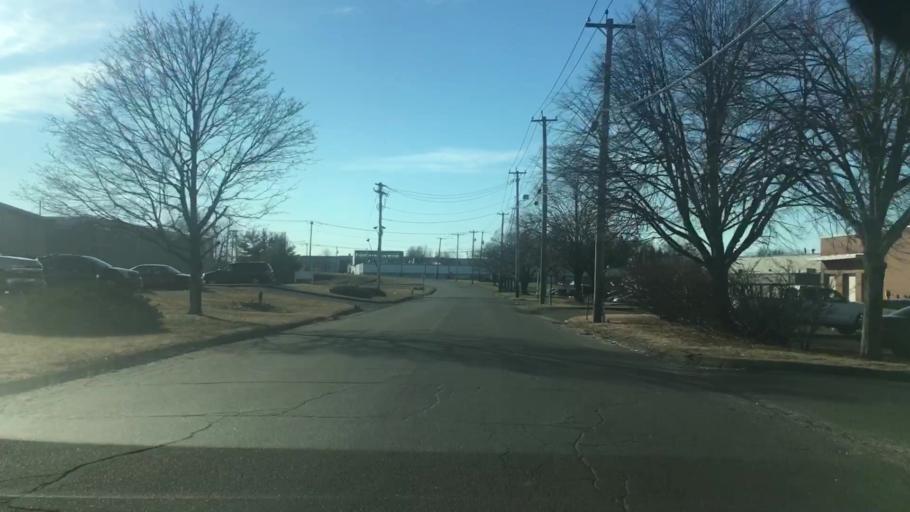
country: US
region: Connecticut
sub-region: New Haven County
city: North Haven
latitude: 41.4204
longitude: -72.8440
